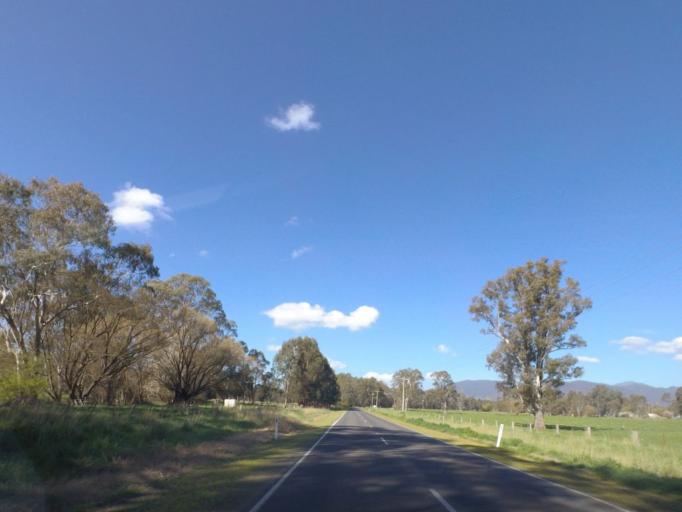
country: AU
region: Victoria
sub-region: Murrindindi
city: Alexandra
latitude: -37.2463
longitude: 145.7777
